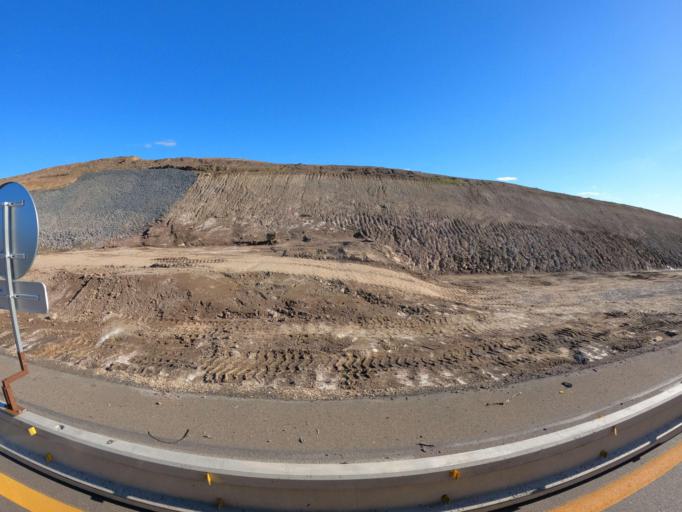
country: FR
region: Bourgogne
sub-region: Departement de Saone-et-Loire
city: Ciry-le-Noble
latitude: 46.6178
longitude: 4.2807
